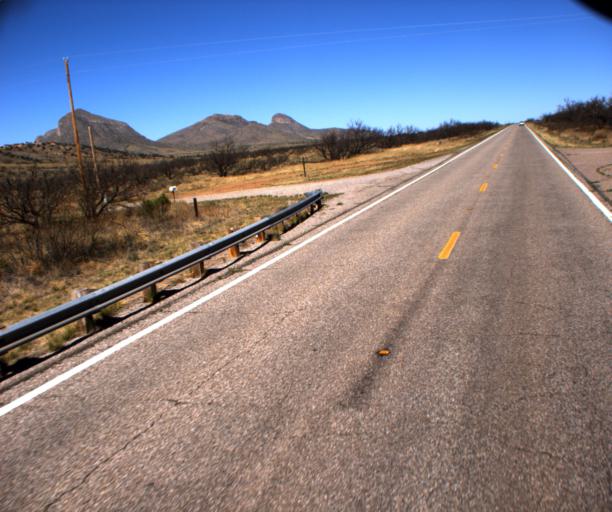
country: US
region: Arizona
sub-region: Cochise County
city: Huachuca City
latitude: 31.6998
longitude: -110.4279
